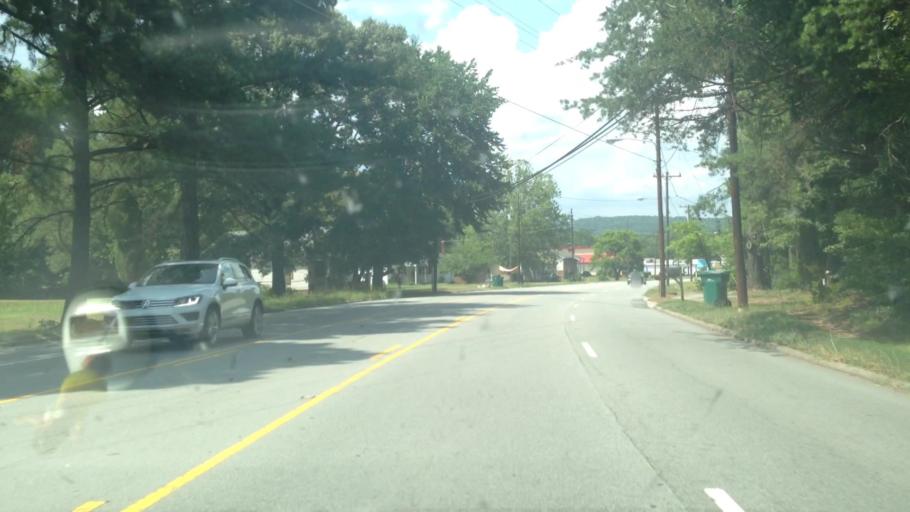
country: US
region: North Carolina
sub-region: Rockingham County
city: Mayodan
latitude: 36.3985
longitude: -79.9706
